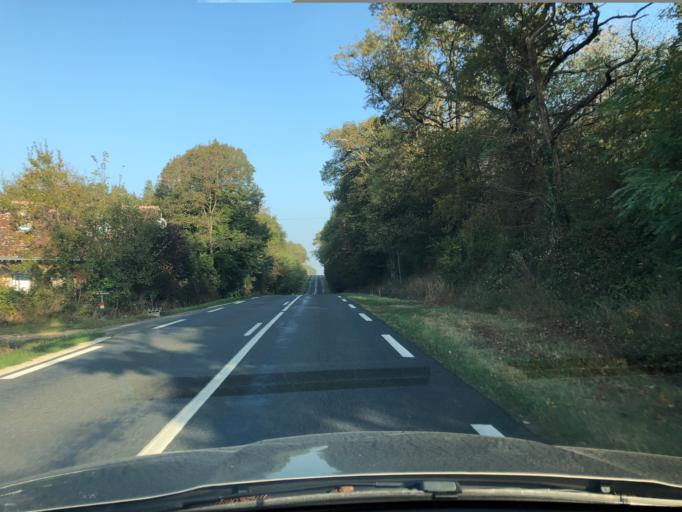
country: FR
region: Centre
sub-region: Departement d'Indre-et-Loire
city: Beaumont-la-Ronce
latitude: 47.6043
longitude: 0.6617
